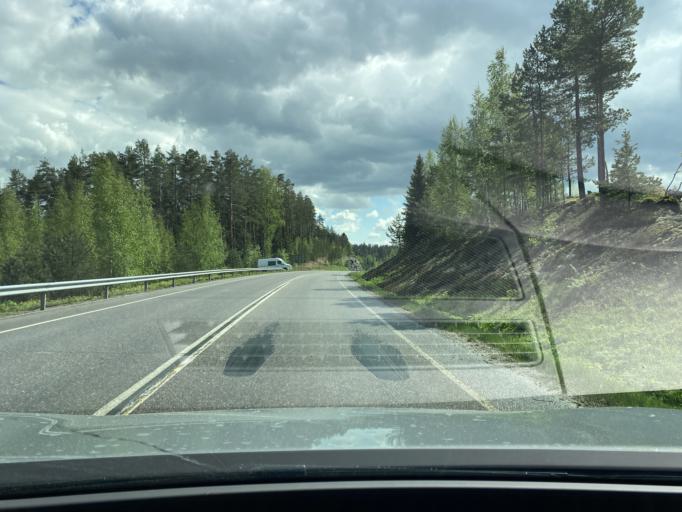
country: FI
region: Paijanne Tavastia
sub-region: Lahti
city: Jaervelae
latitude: 60.8124
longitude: 25.3626
